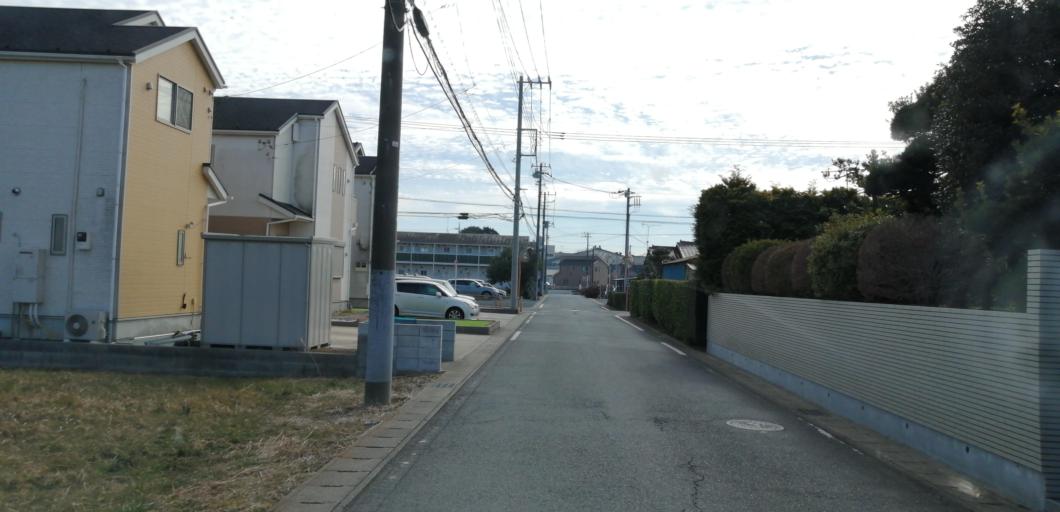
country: JP
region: Chiba
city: Narita
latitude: 35.7368
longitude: 140.3302
